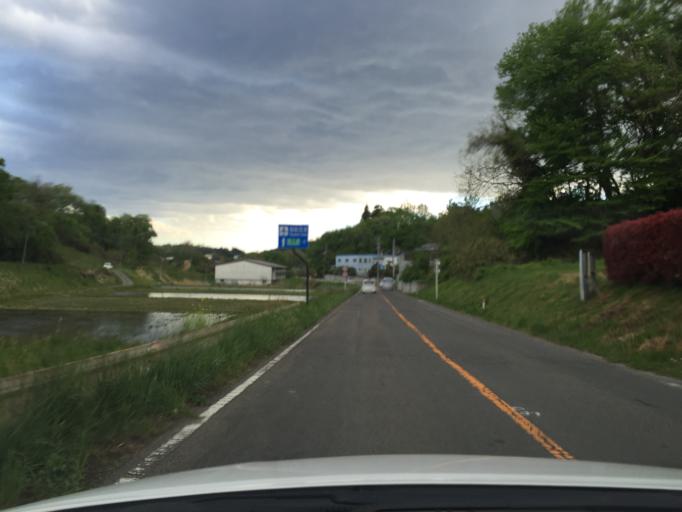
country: JP
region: Fukushima
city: Fukushima-shi
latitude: 37.6641
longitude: 140.5144
